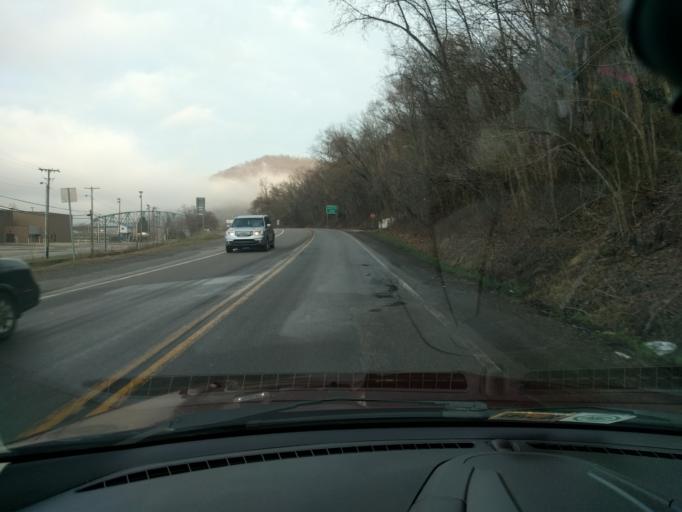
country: US
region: West Virginia
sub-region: Kanawha County
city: Montgomery
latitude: 38.1824
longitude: -81.3088
